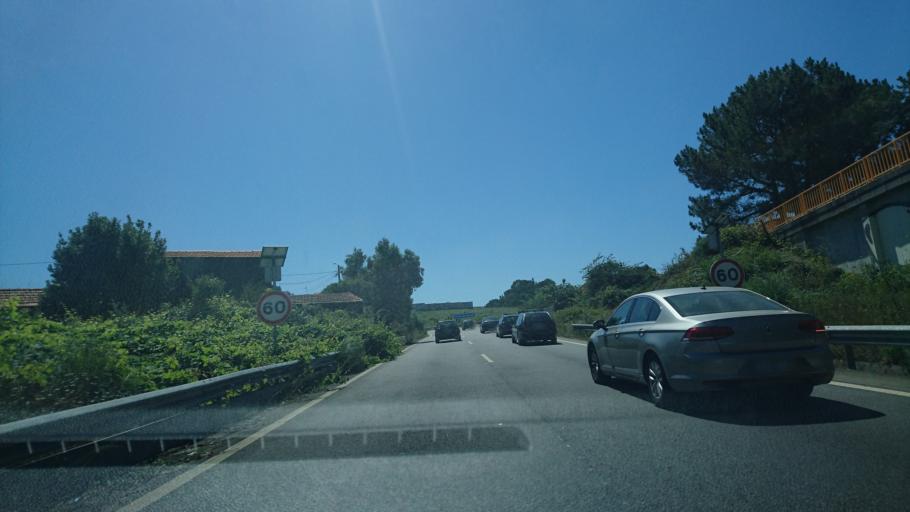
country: PT
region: Porto
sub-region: Vila Nova de Gaia
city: Vila Nova de Gaia
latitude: 41.1178
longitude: -8.6258
